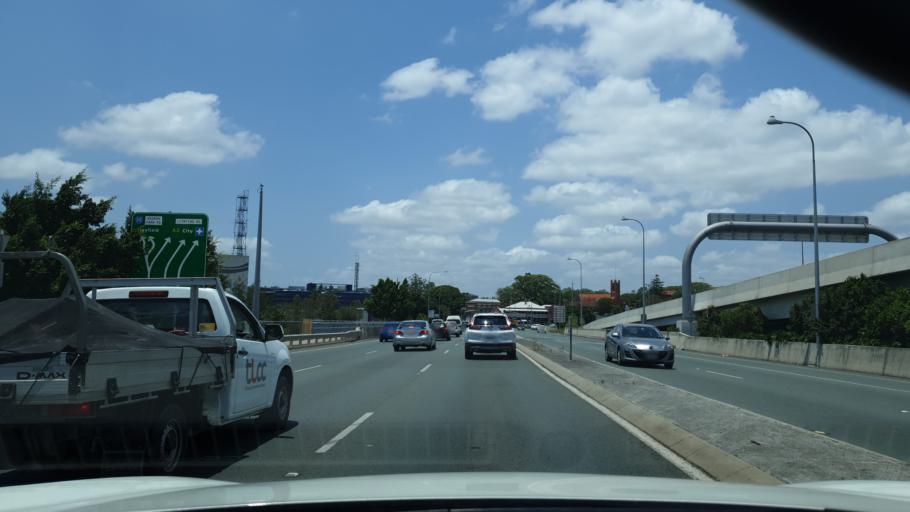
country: AU
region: Queensland
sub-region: Brisbane
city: Gordon Park
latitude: -27.4133
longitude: 153.0347
